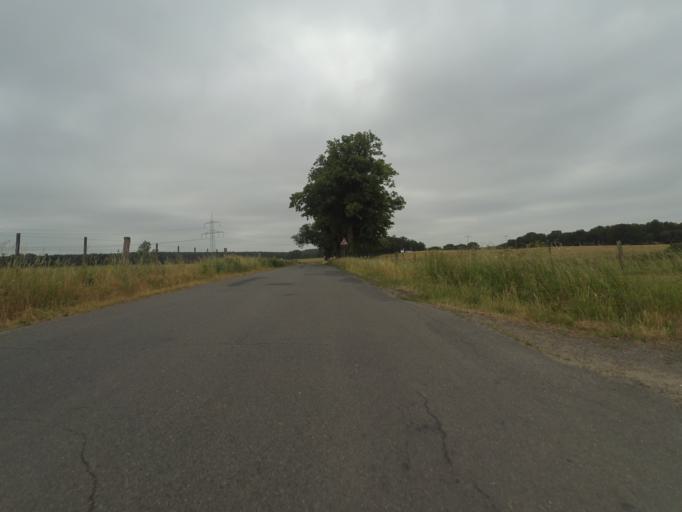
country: DE
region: Mecklenburg-Vorpommern
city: Demen
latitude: 53.6495
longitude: 11.8141
